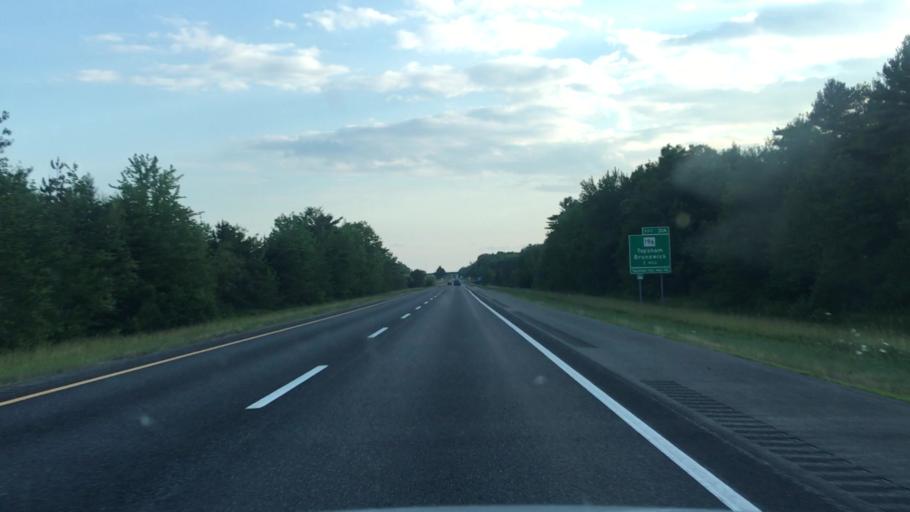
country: US
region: Maine
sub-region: Sagadahoc County
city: Topsham
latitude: 43.9568
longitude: -69.9632
